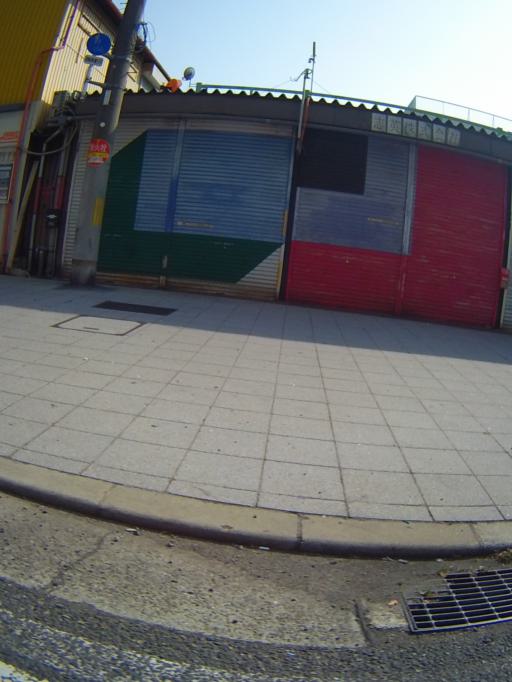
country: JP
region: Osaka
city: Osaka-shi
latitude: 34.6566
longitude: 135.4725
